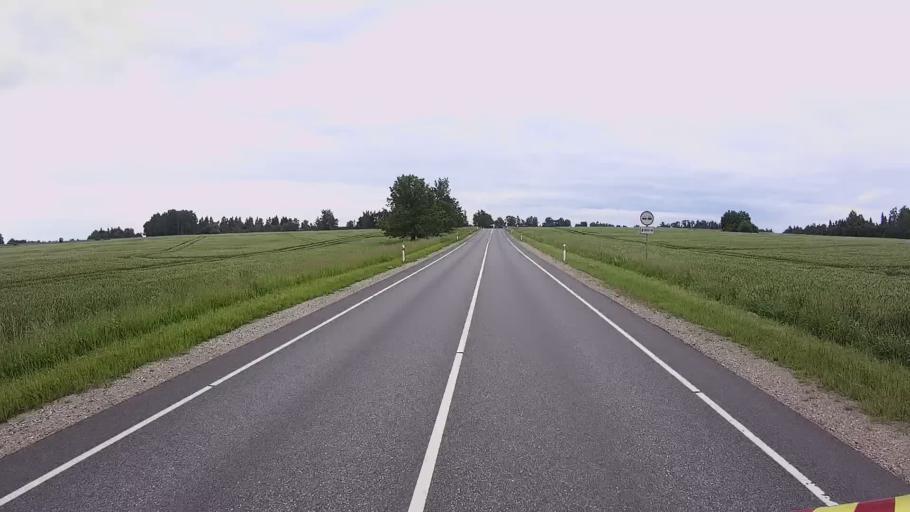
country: EE
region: Viljandimaa
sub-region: Karksi vald
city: Karksi-Nuia
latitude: 58.1392
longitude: 25.5859
